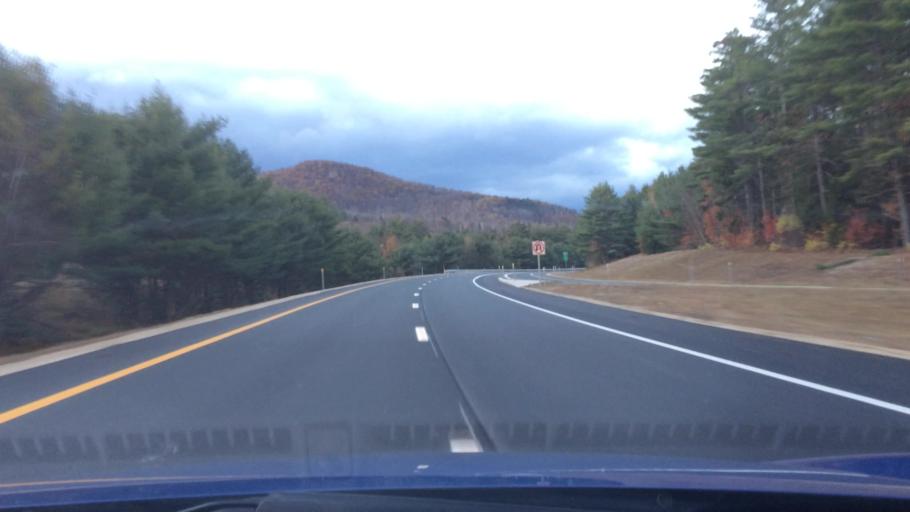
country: US
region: New Hampshire
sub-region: Grafton County
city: Thornton
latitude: 43.8715
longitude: -71.6706
